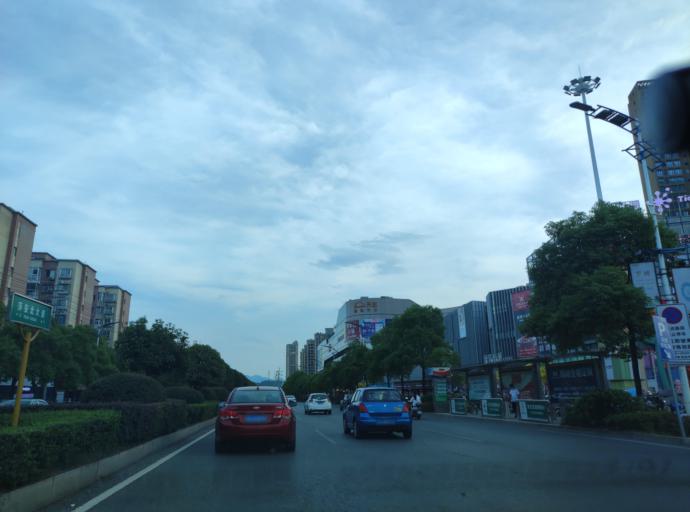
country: CN
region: Jiangxi Sheng
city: Pingxiang
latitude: 27.6373
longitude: 113.8700
